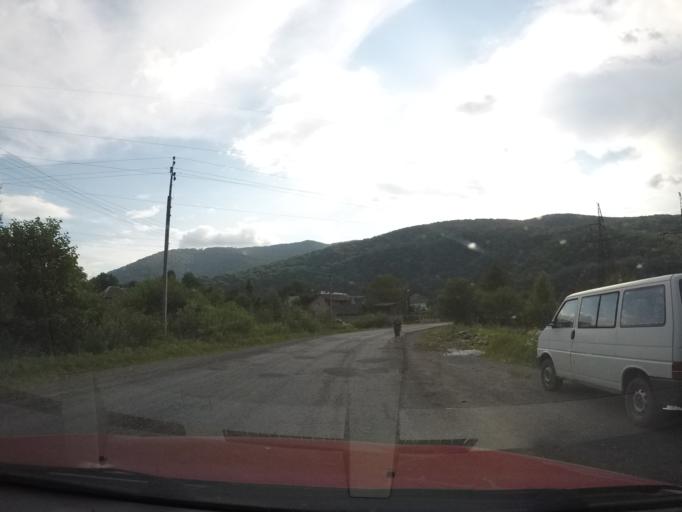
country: UA
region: Zakarpattia
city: Velykyi Bereznyi
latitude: 48.9844
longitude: 22.6334
